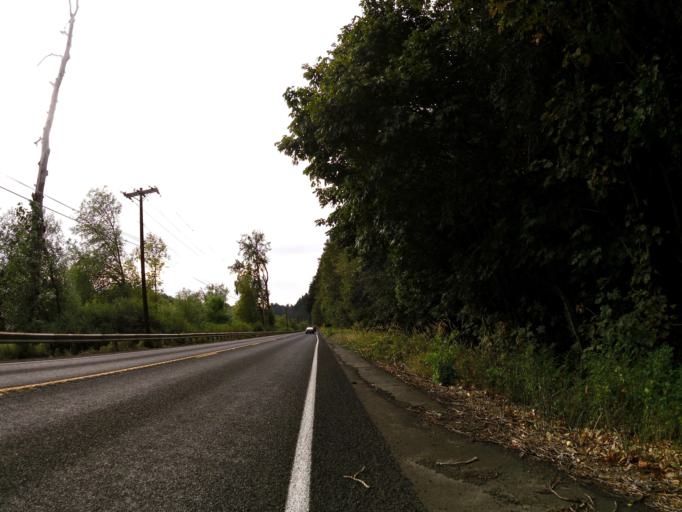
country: US
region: Washington
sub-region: Cowlitz County
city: West Longview
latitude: 46.1886
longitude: -123.1027
